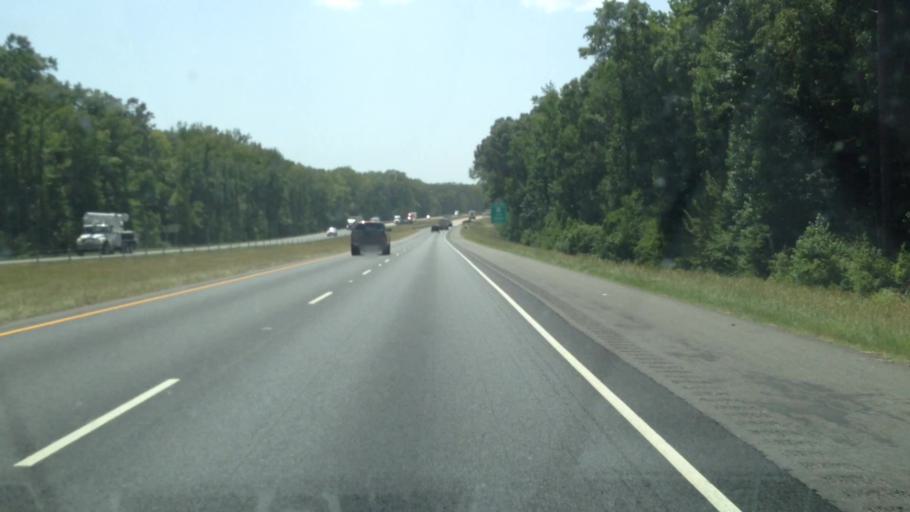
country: US
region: Louisiana
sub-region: Webster Parish
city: Minden
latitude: 32.5619
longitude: -93.1443
